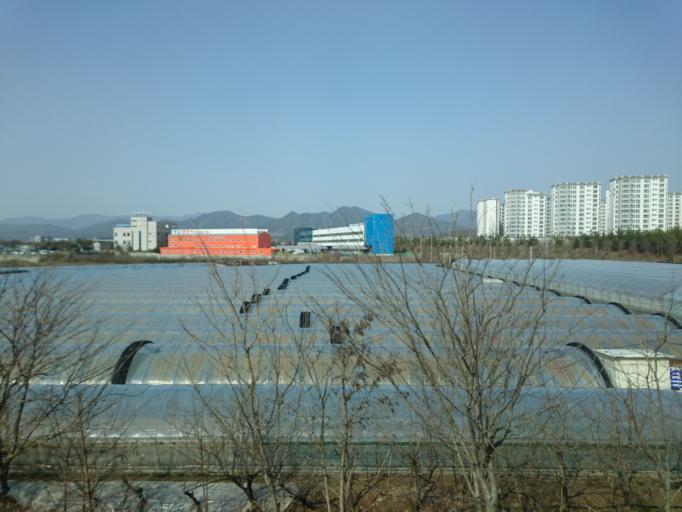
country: KR
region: Gyeongsangbuk-do
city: Gyeongsan-si
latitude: 35.8660
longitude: 128.6843
